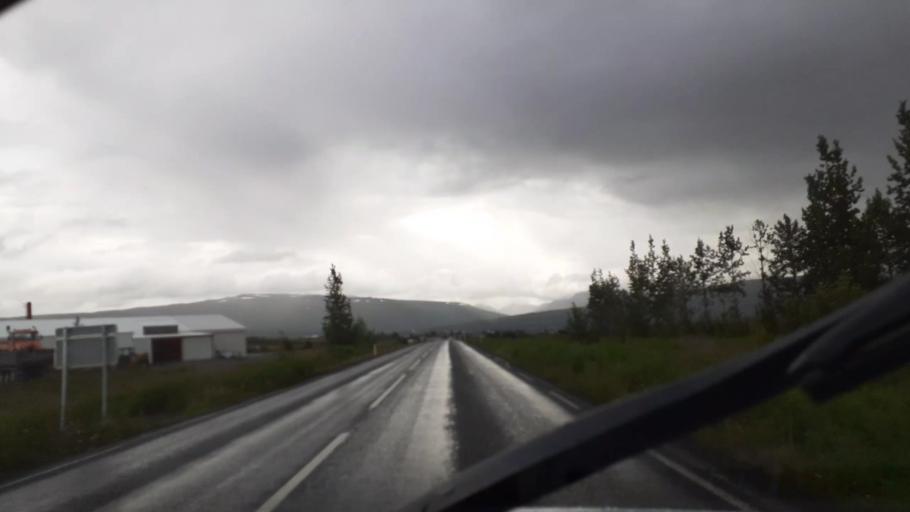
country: IS
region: East
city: Egilsstadir
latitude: 65.2963
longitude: -14.4426
